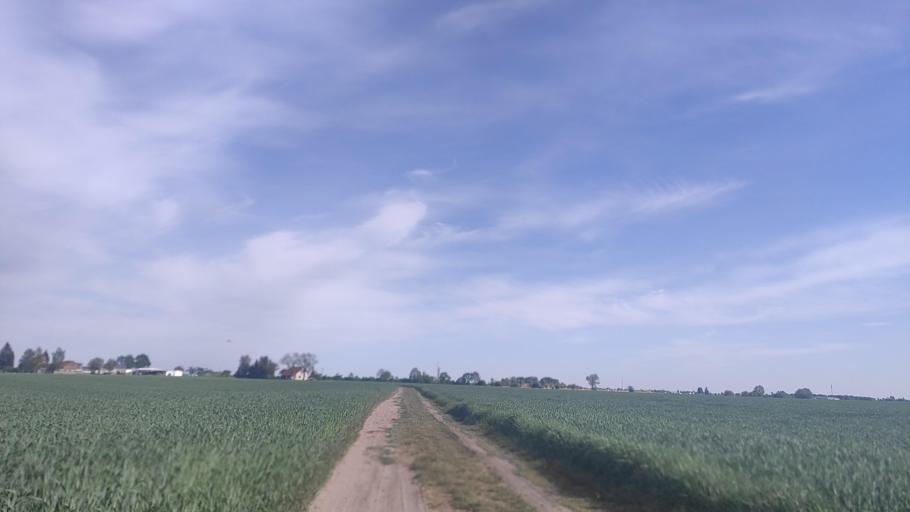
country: PL
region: Greater Poland Voivodeship
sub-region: Powiat poznanski
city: Swarzedz
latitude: 52.4170
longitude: 17.1477
